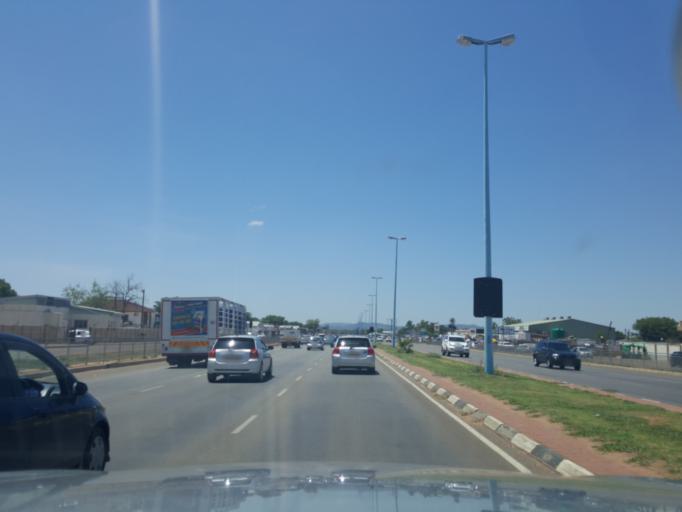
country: BW
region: Kweneng
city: Mogoditshane
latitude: -24.6240
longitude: 25.8688
